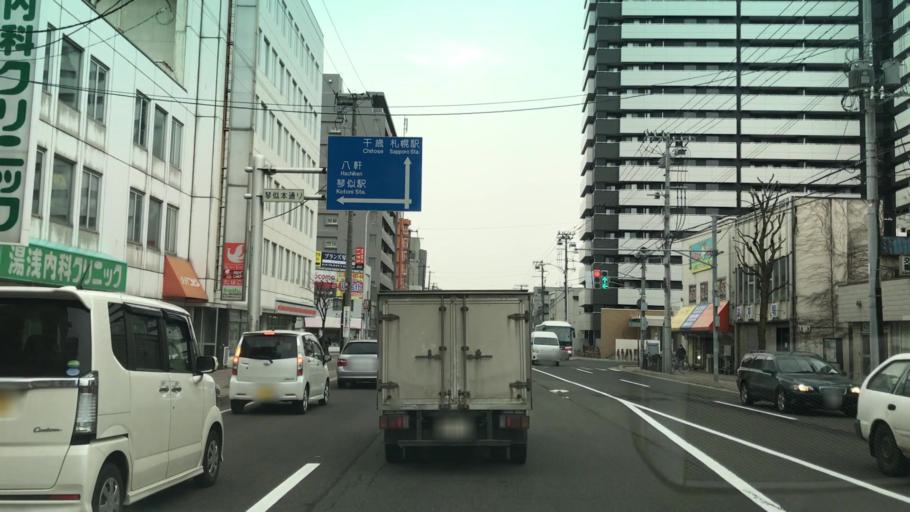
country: JP
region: Hokkaido
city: Sapporo
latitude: 43.0733
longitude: 141.2990
